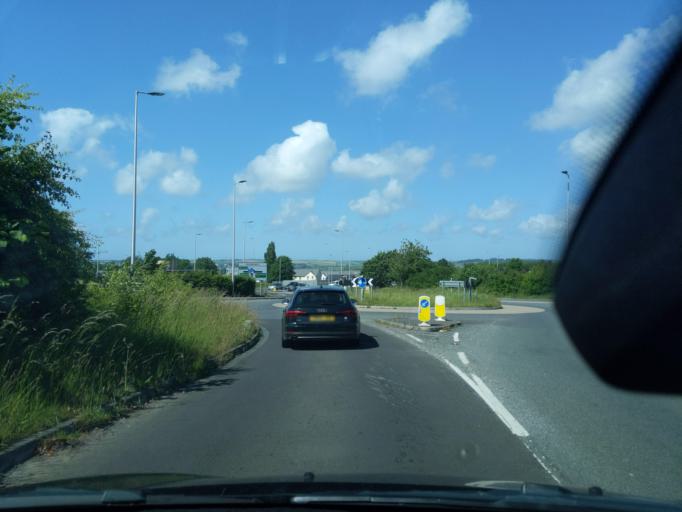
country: GB
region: England
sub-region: Devon
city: Barnstaple
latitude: 51.0611
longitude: -4.0827
